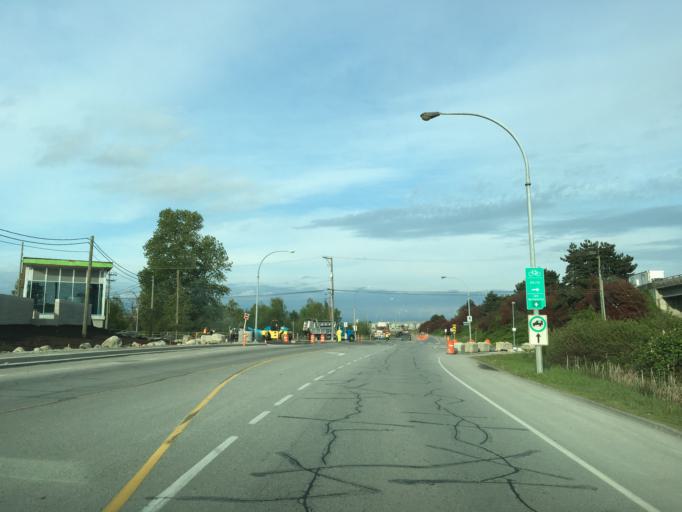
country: CA
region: British Columbia
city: New Westminster
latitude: 49.1835
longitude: -122.9584
